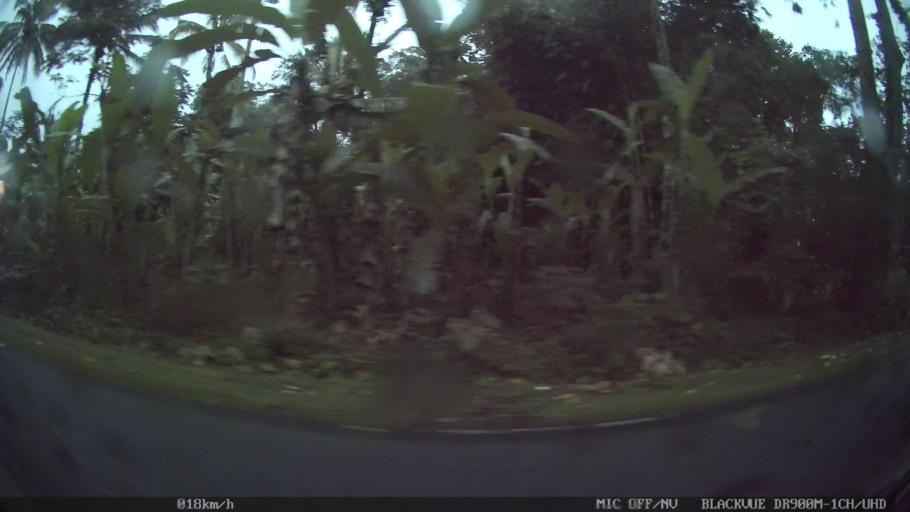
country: ID
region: Bali
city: Banjar Ponggang
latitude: -8.3828
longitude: 115.2643
